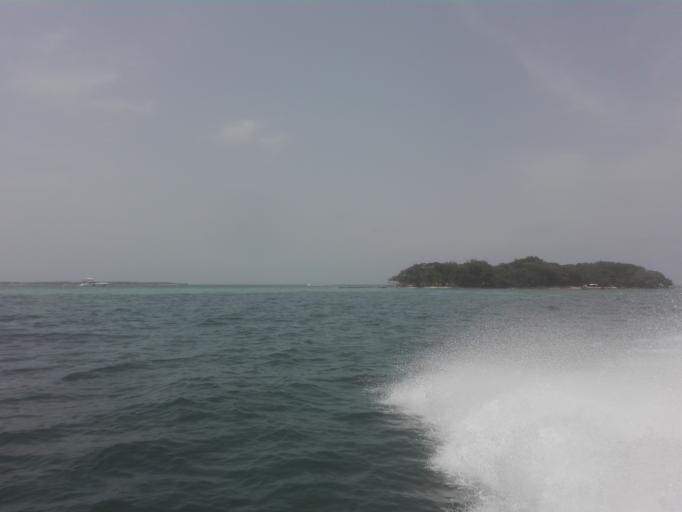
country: CO
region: Bolivar
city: Turbana
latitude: 10.1479
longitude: -75.7288
